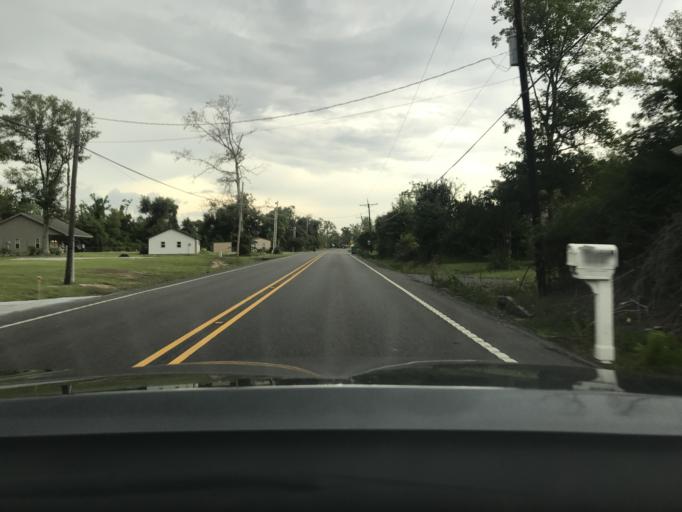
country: US
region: Louisiana
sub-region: Calcasieu Parish
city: Westlake
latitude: 30.2690
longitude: -93.2430
